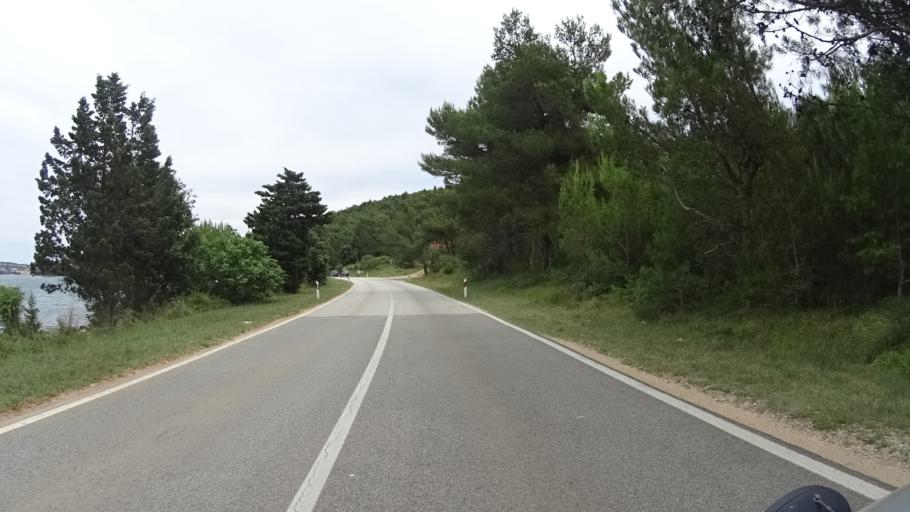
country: HR
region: Istarska
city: Medulin
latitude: 44.8148
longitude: 13.9012
